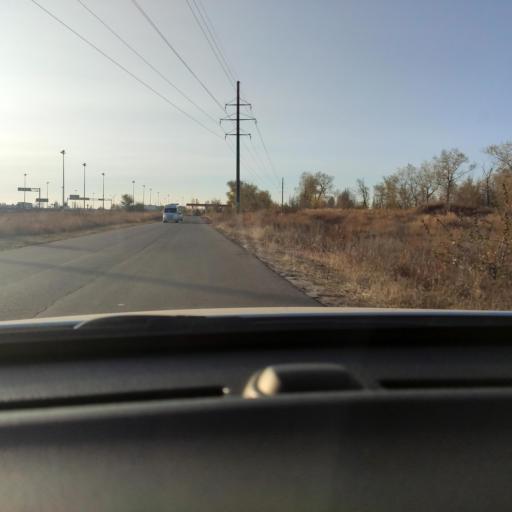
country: RU
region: Voronezj
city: Somovo
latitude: 51.6593
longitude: 39.3013
